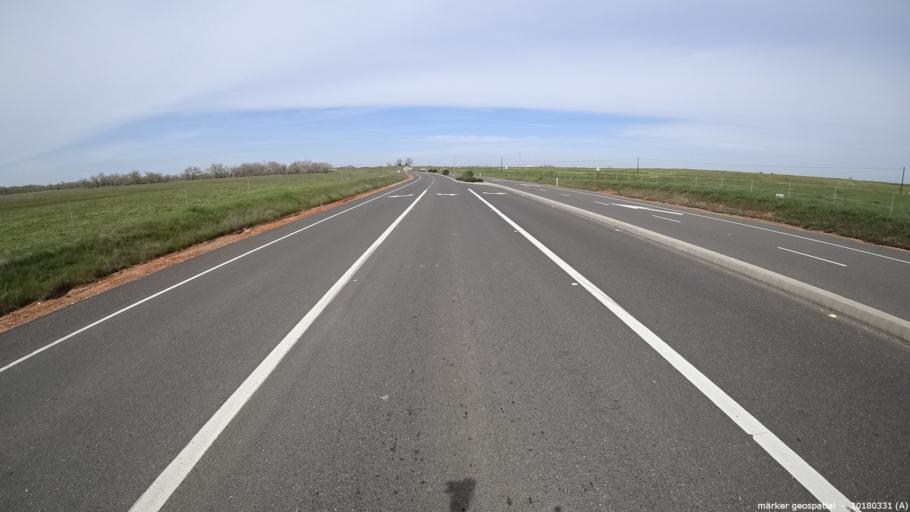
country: US
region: California
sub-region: Sacramento County
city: Gold River
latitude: 38.5946
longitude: -121.1783
